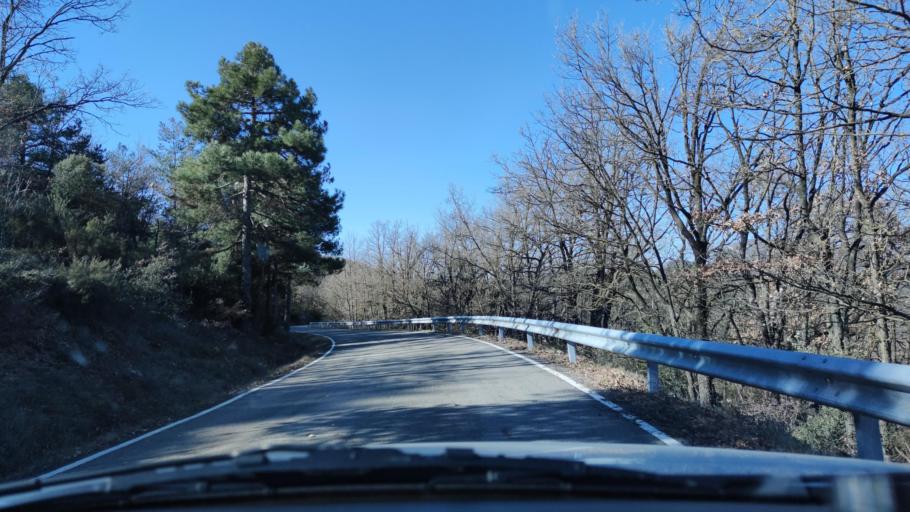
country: ES
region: Catalonia
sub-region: Provincia de Lleida
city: Artesa de Segre
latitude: 42.0503
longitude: 1.0767
